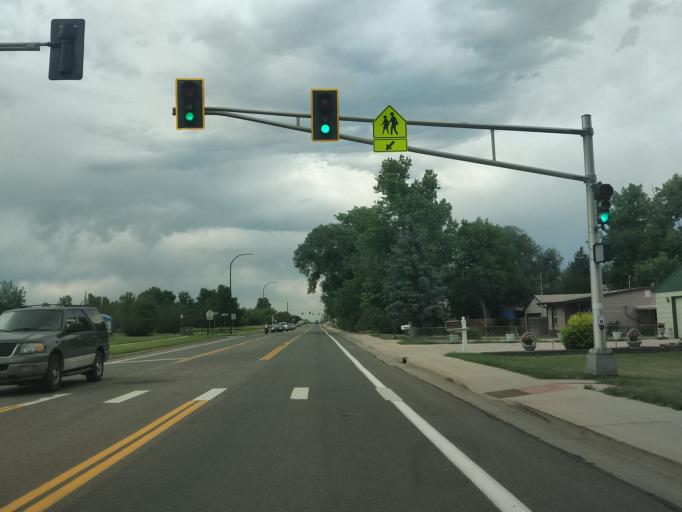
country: US
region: Colorado
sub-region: Jefferson County
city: Lakewood
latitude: 39.7011
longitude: -105.1002
